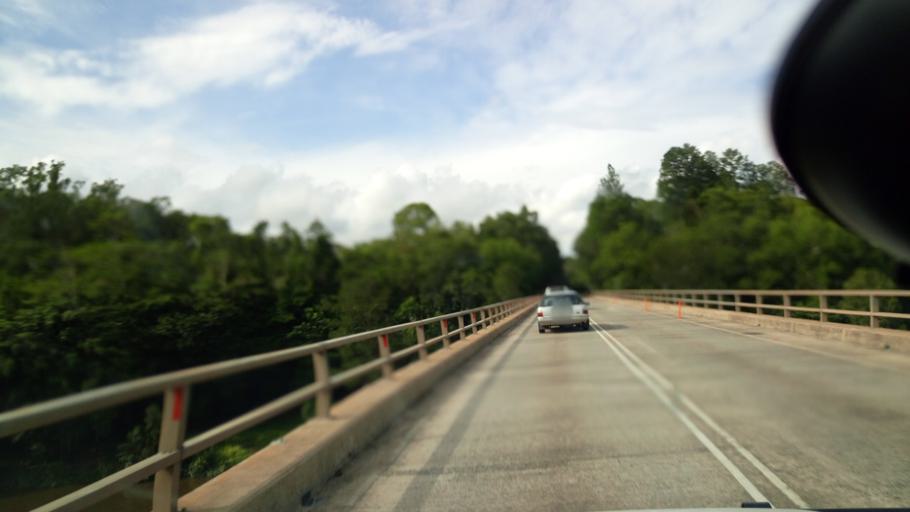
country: AU
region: Queensland
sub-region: Tablelands
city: Kuranda
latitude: -16.8156
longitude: 145.6345
